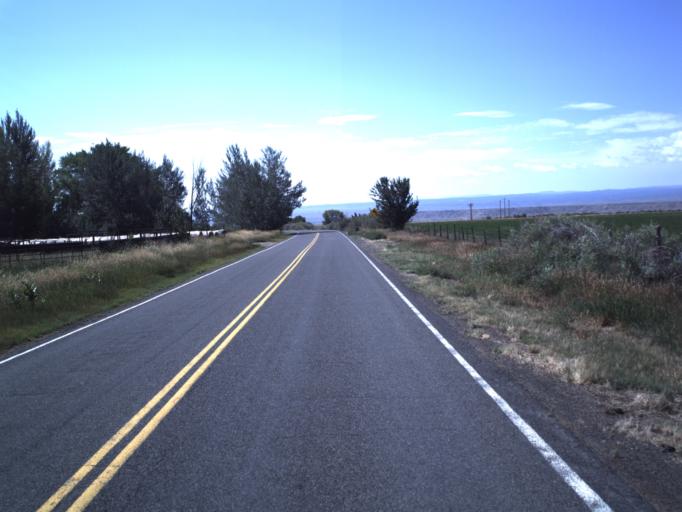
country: US
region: Utah
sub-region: Duchesne County
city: Duchesne
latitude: 40.2664
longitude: -110.2186
